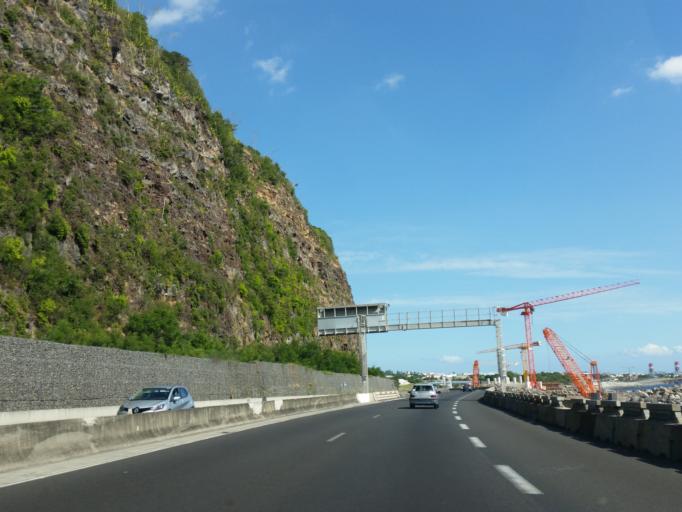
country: RE
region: Reunion
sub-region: Reunion
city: La Possession
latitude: -20.9188
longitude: 55.3484
